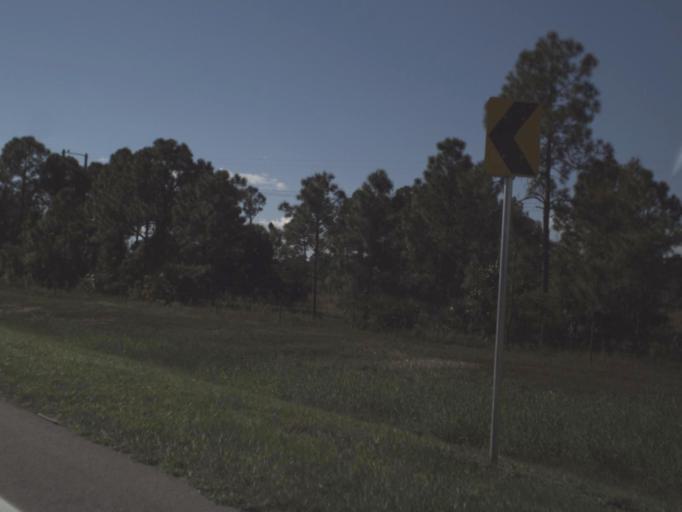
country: US
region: Florida
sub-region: Lee County
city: Lehigh Acres
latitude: 26.5388
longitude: -81.6338
